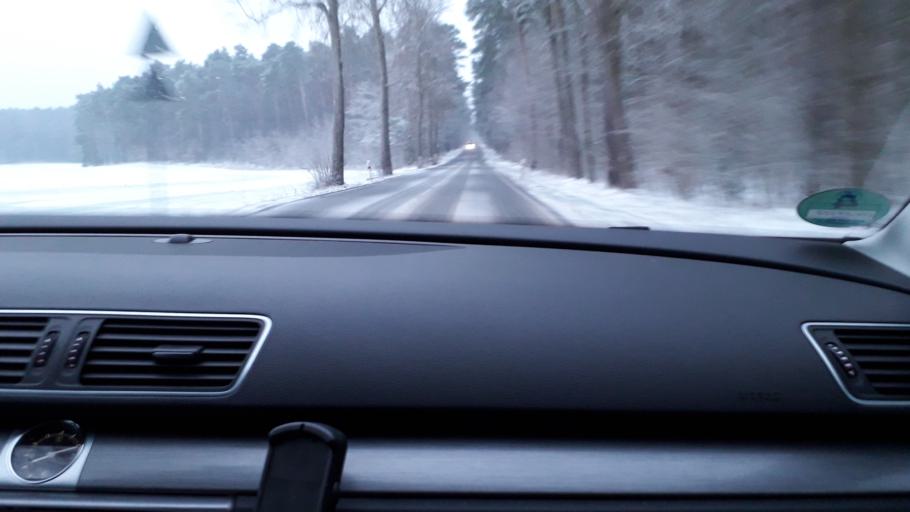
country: DE
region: Brandenburg
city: Spremberg
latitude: 51.5934
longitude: 14.4368
